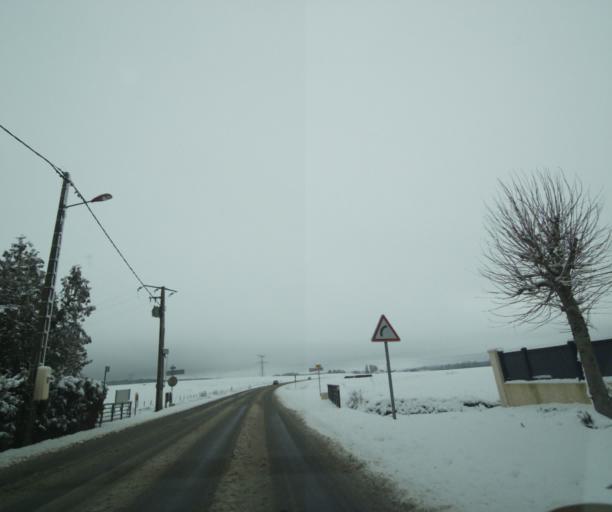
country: FR
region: Champagne-Ardenne
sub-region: Departement de la Haute-Marne
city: Wassy
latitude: 48.5234
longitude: 4.9312
